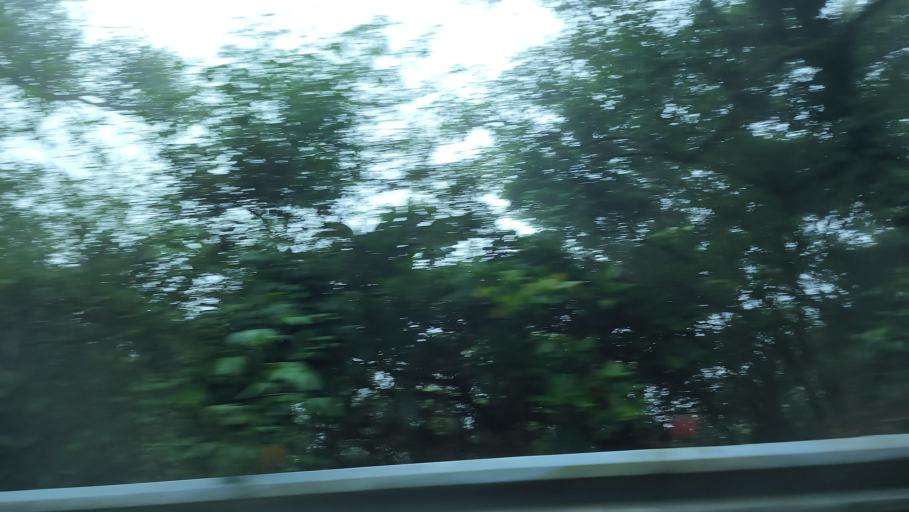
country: TW
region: Taipei
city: Taipei
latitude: 25.1418
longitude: 121.6032
